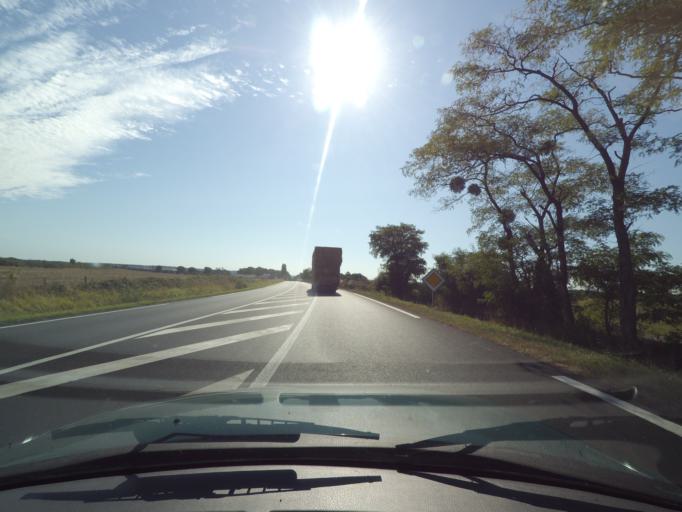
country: FR
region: Poitou-Charentes
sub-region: Departement de la Vienne
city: Lussac-les-Chateaux
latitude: 46.4148
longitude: 0.6547
